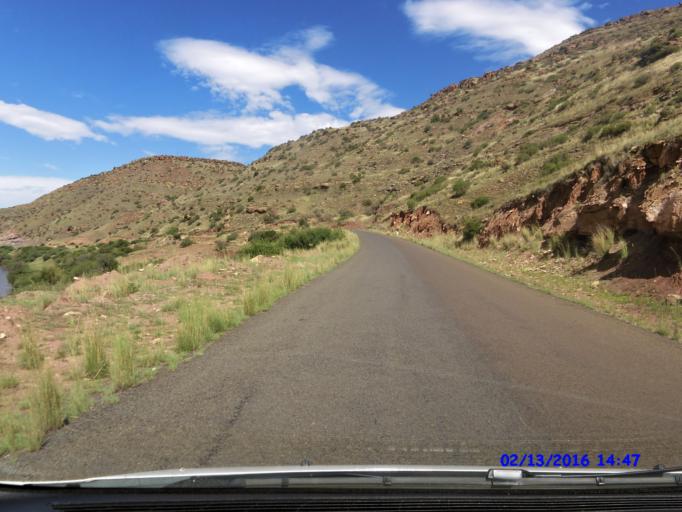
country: LS
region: Qacha's Nek
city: Qacha's Nek
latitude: -30.0675
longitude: 28.4133
